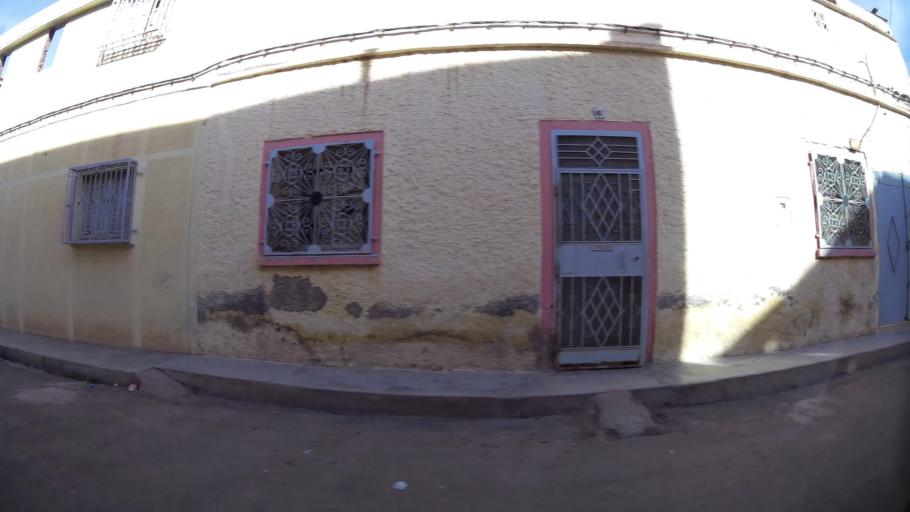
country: MA
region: Oriental
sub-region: Oujda-Angad
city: Oujda
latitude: 34.6724
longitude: -1.8991
